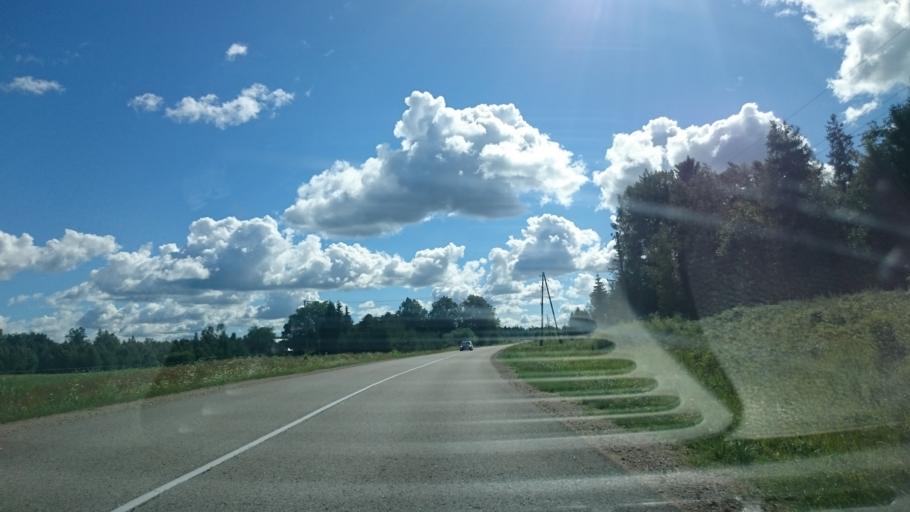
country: LV
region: Kuldigas Rajons
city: Kuldiga
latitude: 56.9074
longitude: 21.9031
